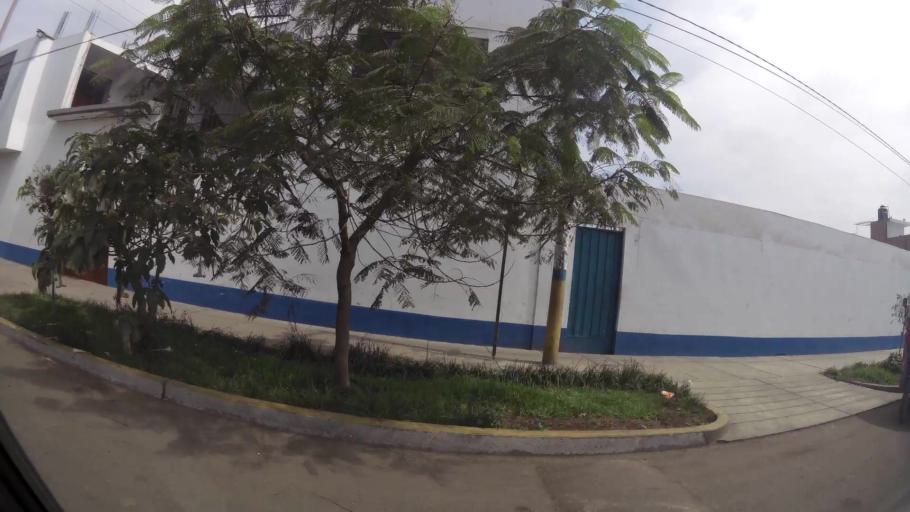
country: PE
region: Lima
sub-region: Provincia de Huaral
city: Huaral
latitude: -11.4959
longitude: -77.2152
